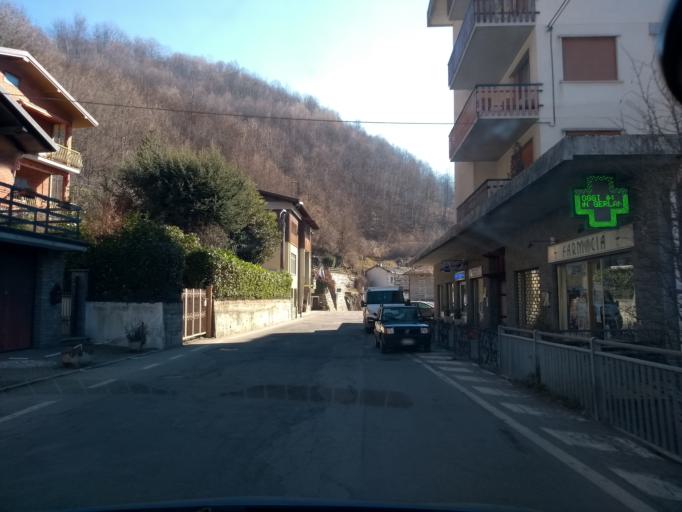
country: IT
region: Piedmont
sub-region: Provincia di Torino
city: Mezzenile
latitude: 45.2907
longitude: 7.4020
